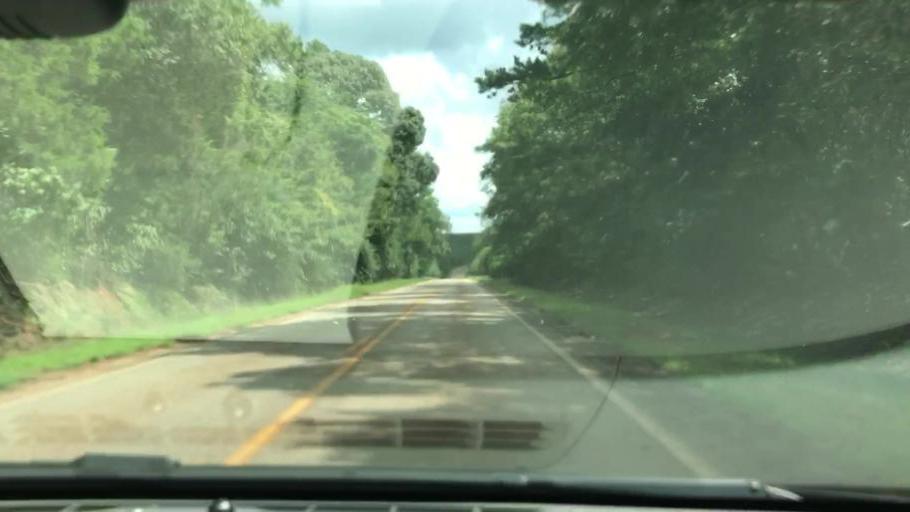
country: US
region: Georgia
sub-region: Stewart County
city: Lumpkin
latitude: 32.0708
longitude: -84.8819
